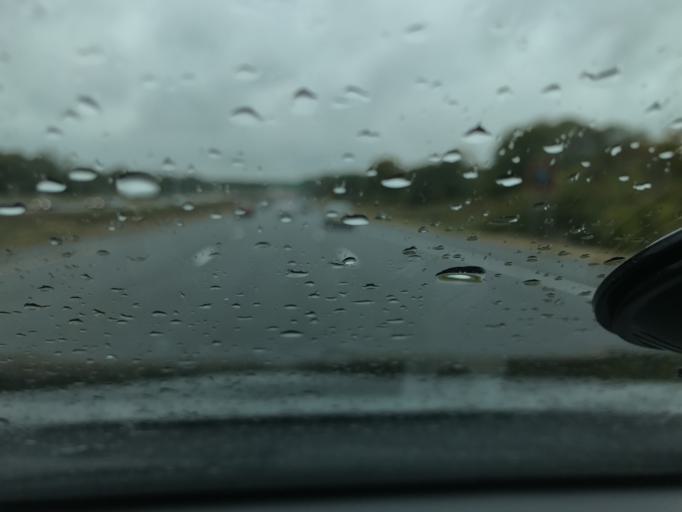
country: US
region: Massachusetts
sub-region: Essex County
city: South Peabody
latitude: 42.5248
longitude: -70.9774
